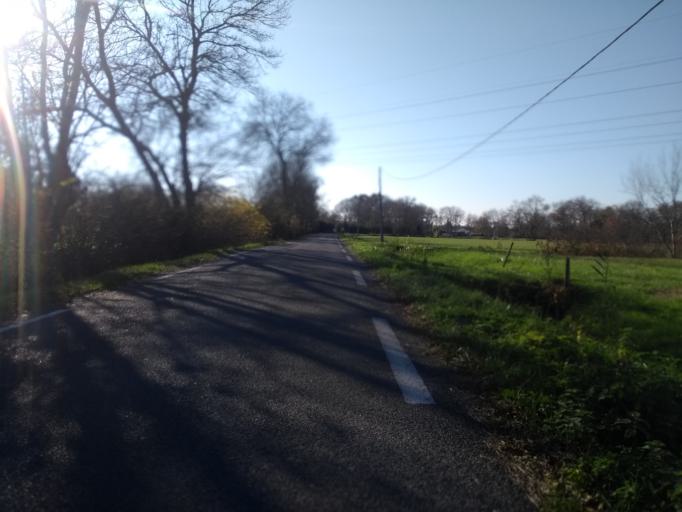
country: FR
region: Aquitaine
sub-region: Departement de la Gironde
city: Ayguemorte-les-Graves
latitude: 44.7257
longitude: -0.4783
